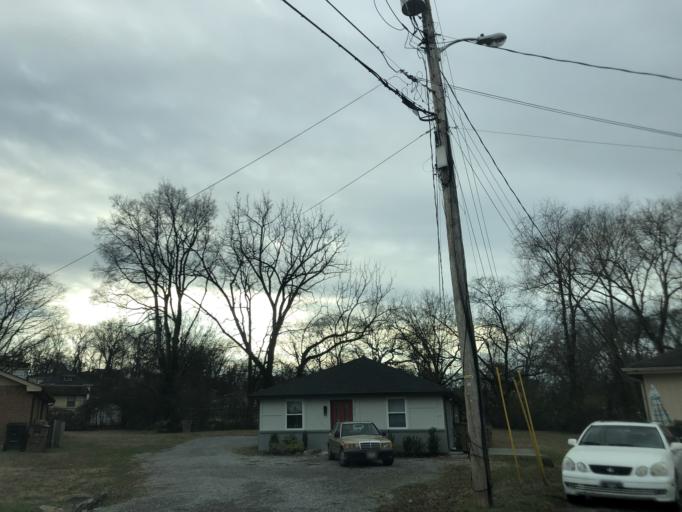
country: US
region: Tennessee
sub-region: Davidson County
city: Nashville
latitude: 36.2024
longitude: -86.7297
